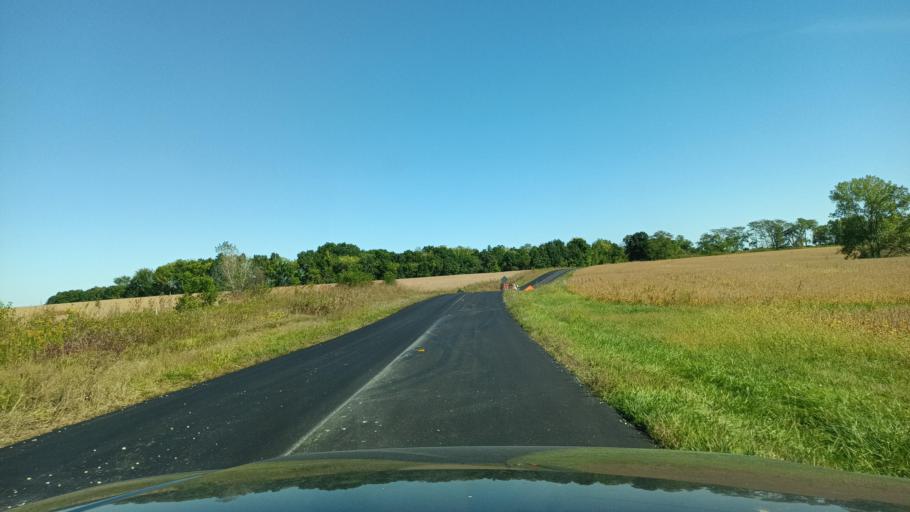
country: US
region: Missouri
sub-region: Macon County
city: La Plata
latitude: 39.9269
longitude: -92.5404
